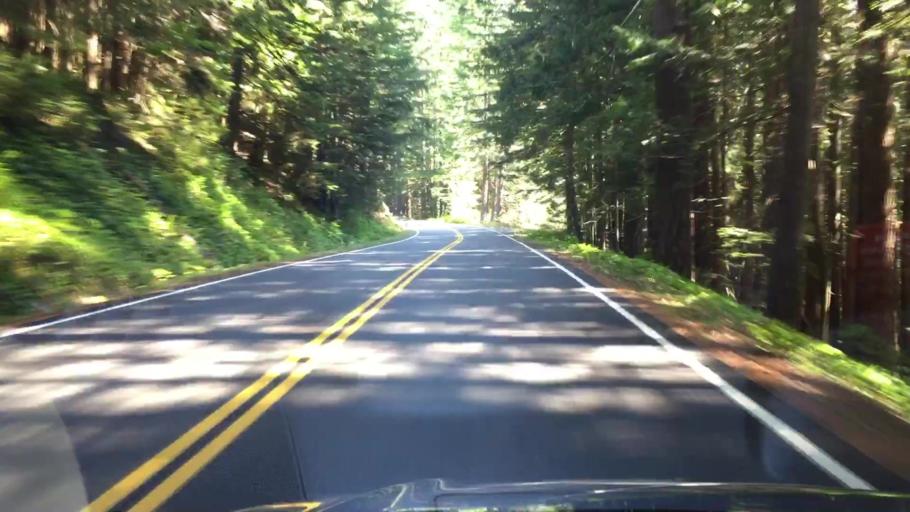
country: US
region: Washington
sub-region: Pierce County
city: Eatonville
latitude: 46.7347
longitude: -121.8744
